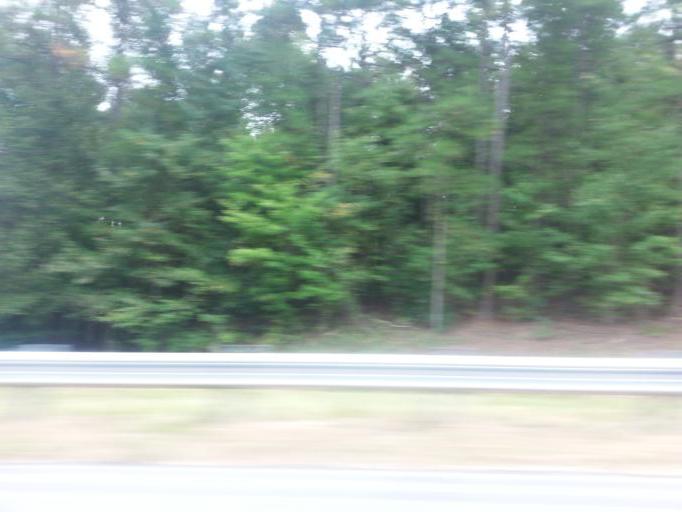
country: US
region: Alabama
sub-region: Conecuh County
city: Evergreen
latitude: 31.4937
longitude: -86.9349
